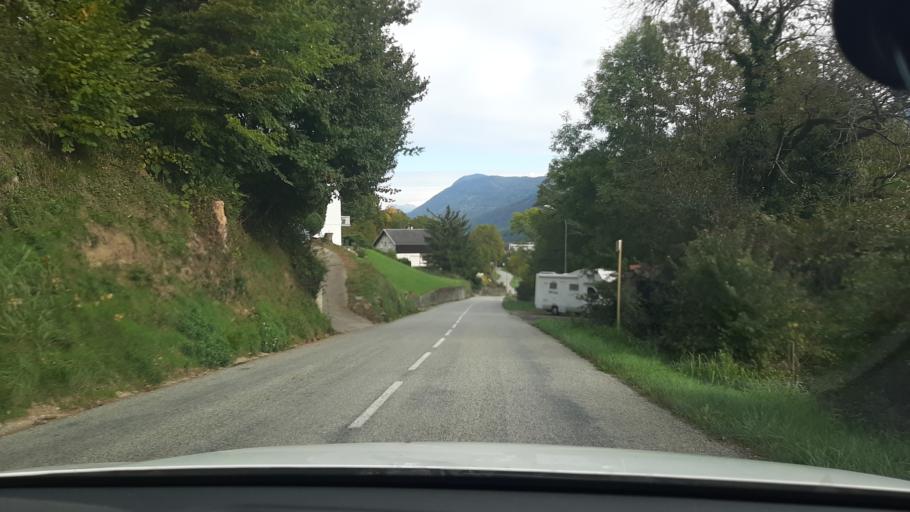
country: FR
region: Rhone-Alpes
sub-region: Departement de la Savoie
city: La Rochette
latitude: 45.4532
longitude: 6.0982
